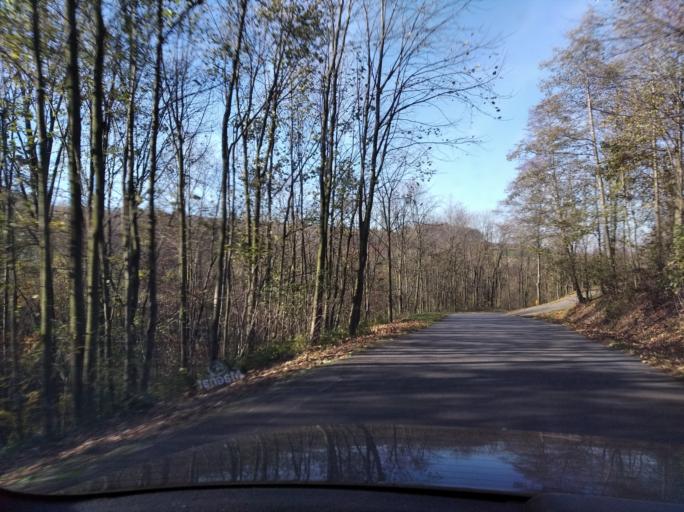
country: PL
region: Subcarpathian Voivodeship
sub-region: Powiat ropczycko-sedziszowski
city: Wielopole Skrzynskie
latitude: 49.9003
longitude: 21.5723
